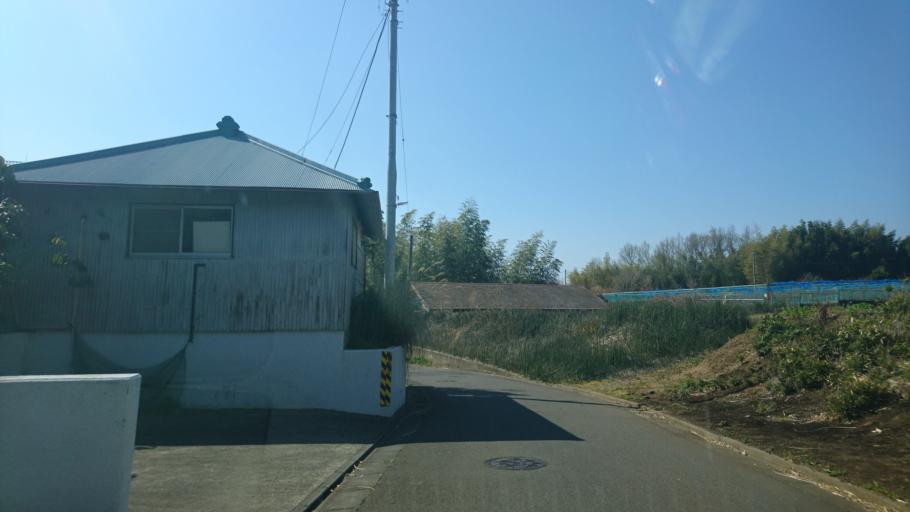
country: JP
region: Kanagawa
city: Fujisawa
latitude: 35.3950
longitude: 139.4372
